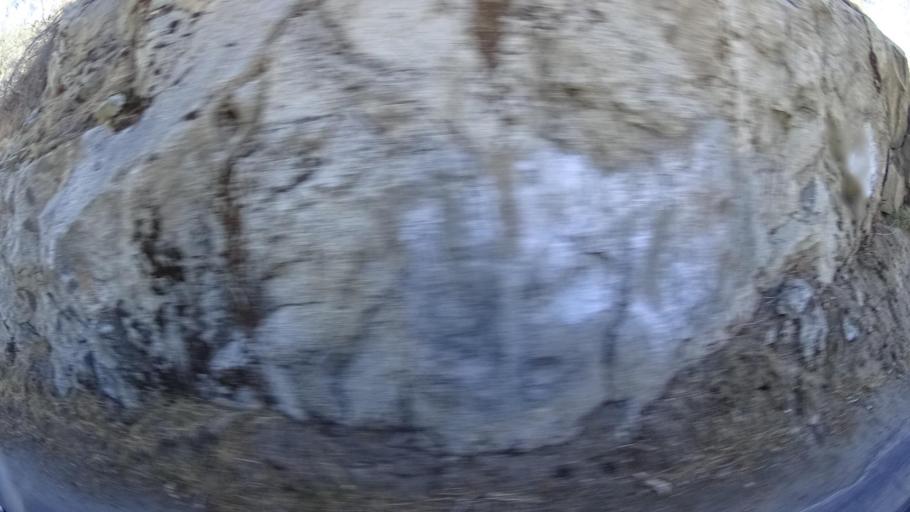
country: US
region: California
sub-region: Kern County
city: Bodfish
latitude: 35.5746
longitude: -118.5486
